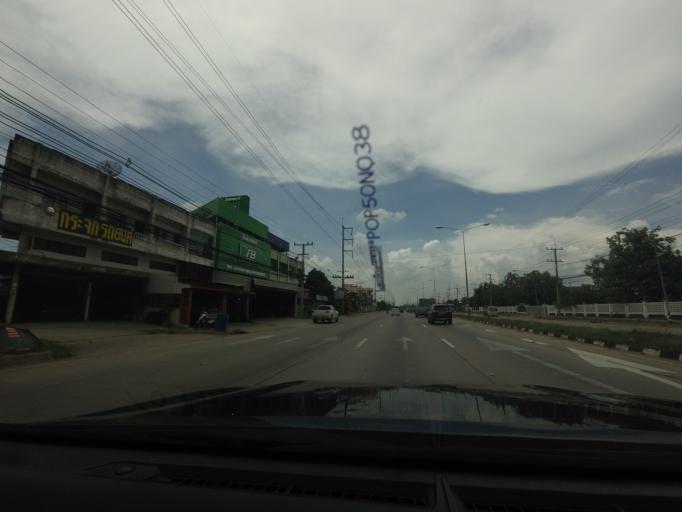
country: TH
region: Nakhon Pathom
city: Nakhon Pathom
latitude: 13.8578
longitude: 100.0131
